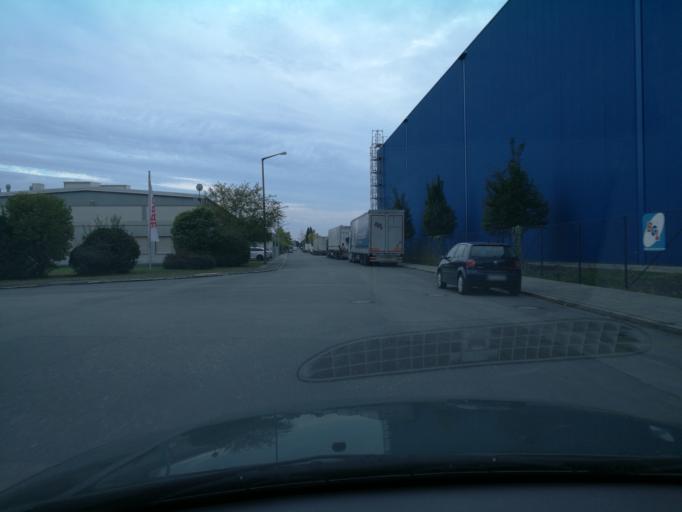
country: DE
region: Bavaria
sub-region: Regierungsbezirk Mittelfranken
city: Furth
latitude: 49.5206
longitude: 11.0021
